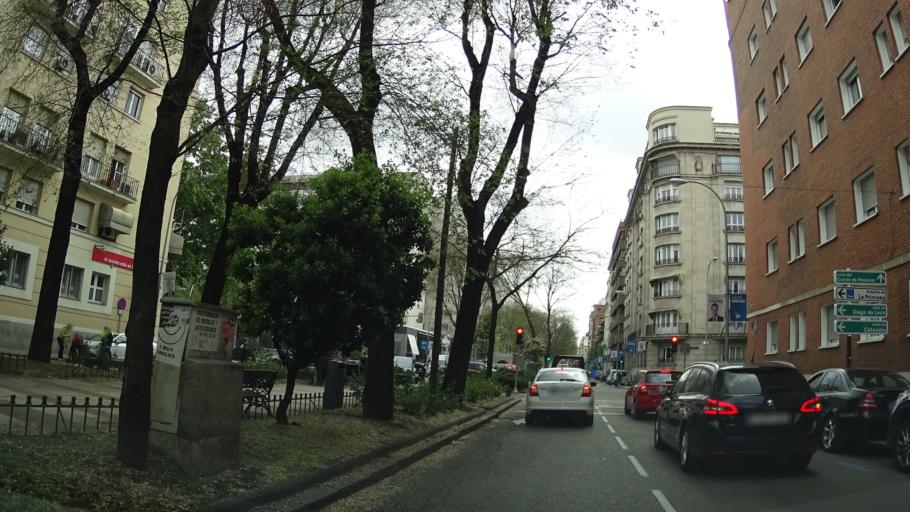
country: ES
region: Madrid
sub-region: Provincia de Madrid
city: Salamanca
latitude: 40.4326
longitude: -3.6800
